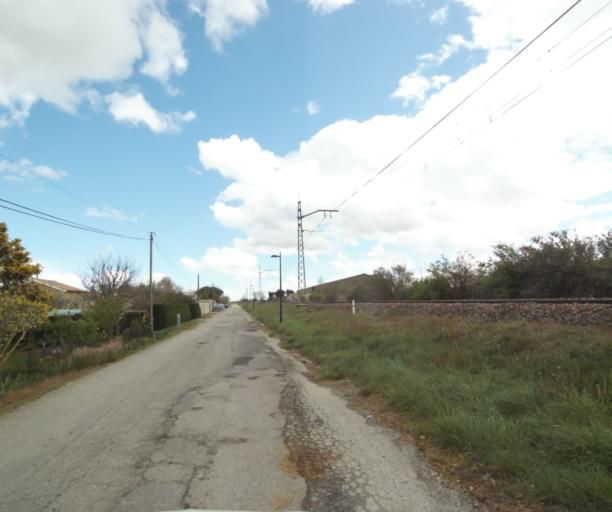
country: FR
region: Midi-Pyrenees
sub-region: Departement de l'Ariege
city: Saverdun
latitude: 43.2362
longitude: 1.5836
